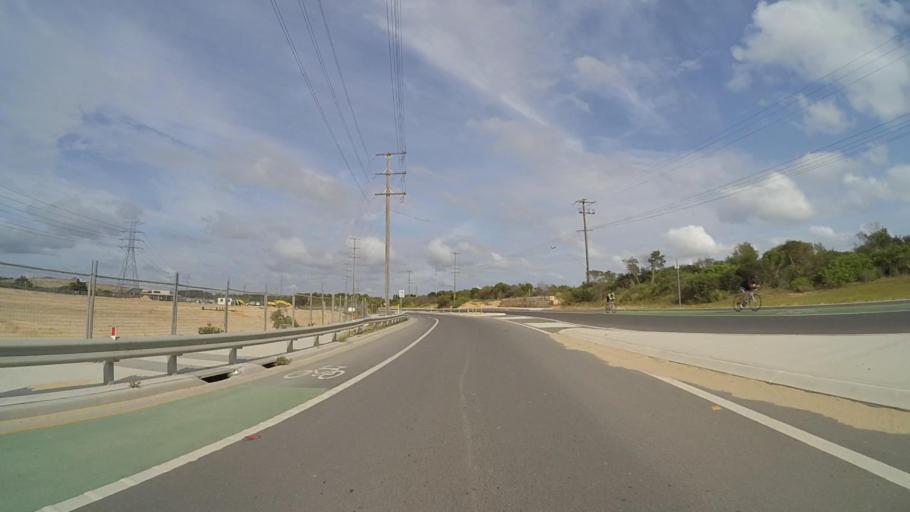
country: AU
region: New South Wales
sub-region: Sutherland Shire
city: Kurnell
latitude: -34.0245
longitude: 151.1858
